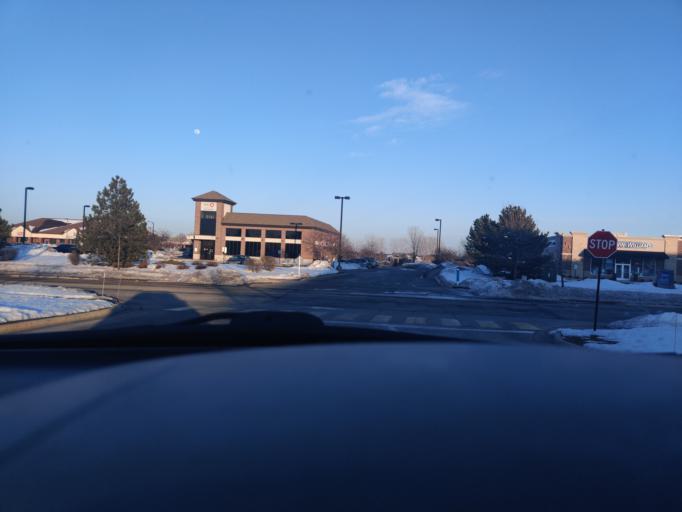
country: US
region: Wisconsin
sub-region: Kenosha County
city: Pleasant Prairie
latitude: 42.5647
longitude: -87.9185
